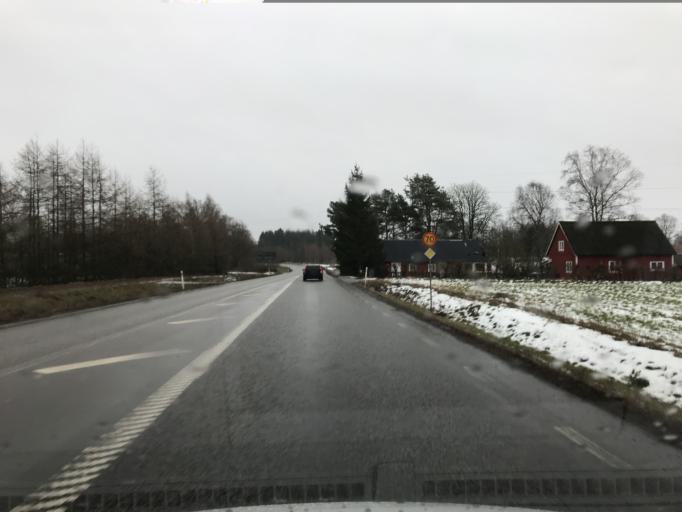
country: SE
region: Skane
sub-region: Hassleholms Kommun
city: Tormestorp
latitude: 56.1745
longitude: 13.6884
